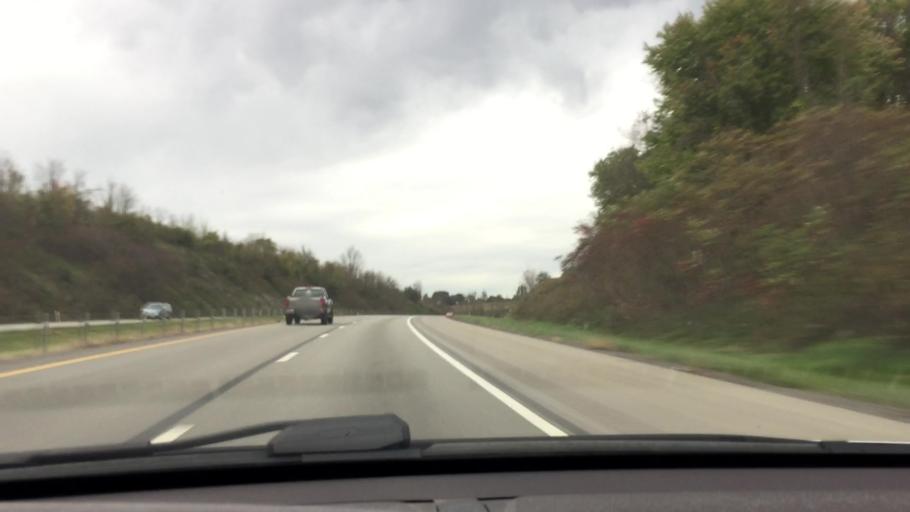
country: US
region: Pennsylvania
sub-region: Beaver County
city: Beaver Falls
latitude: 40.7350
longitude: -80.3709
